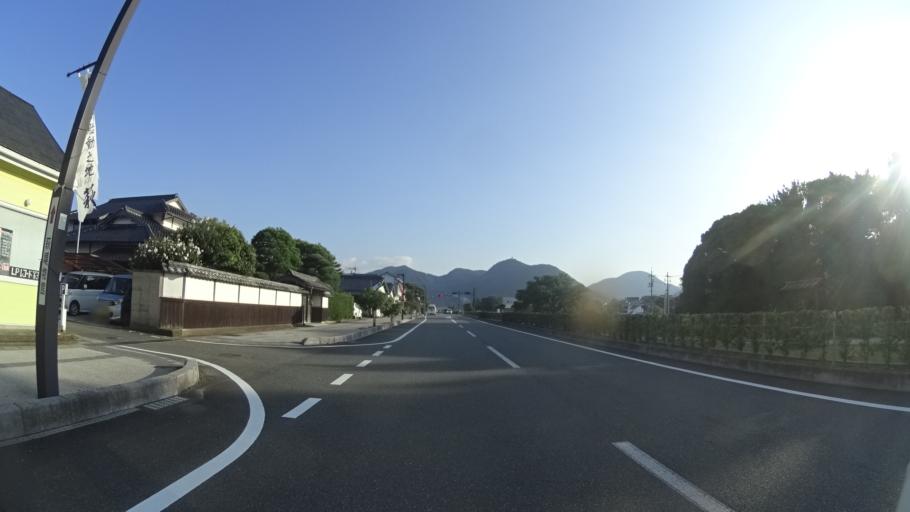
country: JP
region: Yamaguchi
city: Hagi
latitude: 34.4144
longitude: 131.3925
